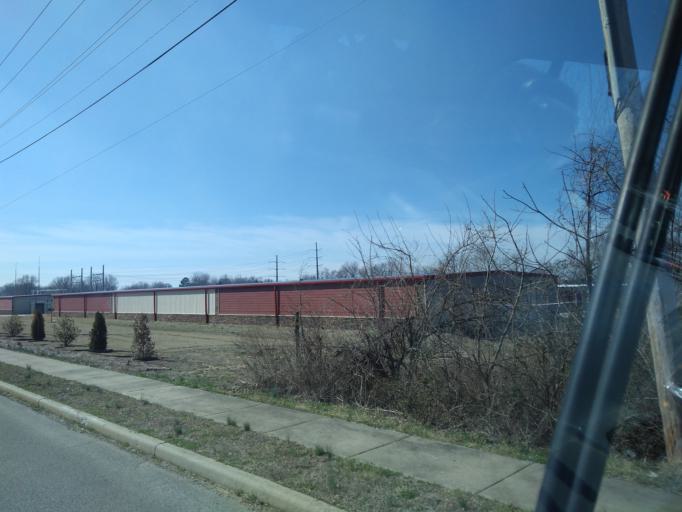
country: US
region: Arkansas
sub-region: Washington County
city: Farmington
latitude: 36.0537
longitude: -94.2359
